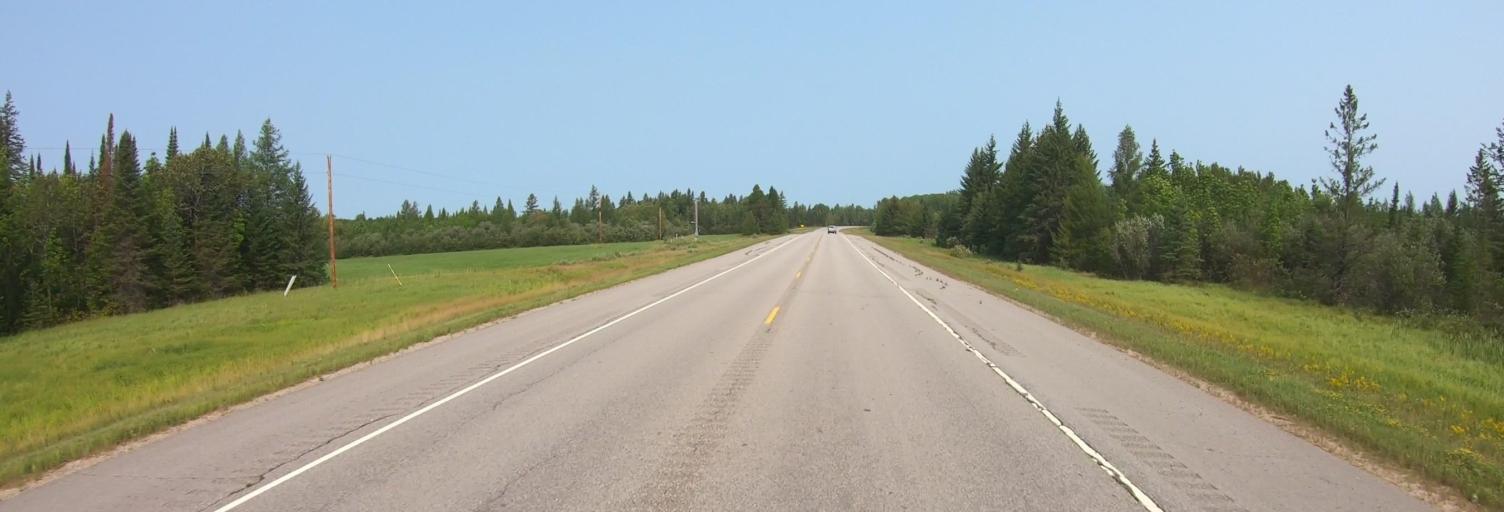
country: CA
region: Ontario
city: Fort Frances
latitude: 48.2930
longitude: -92.9699
